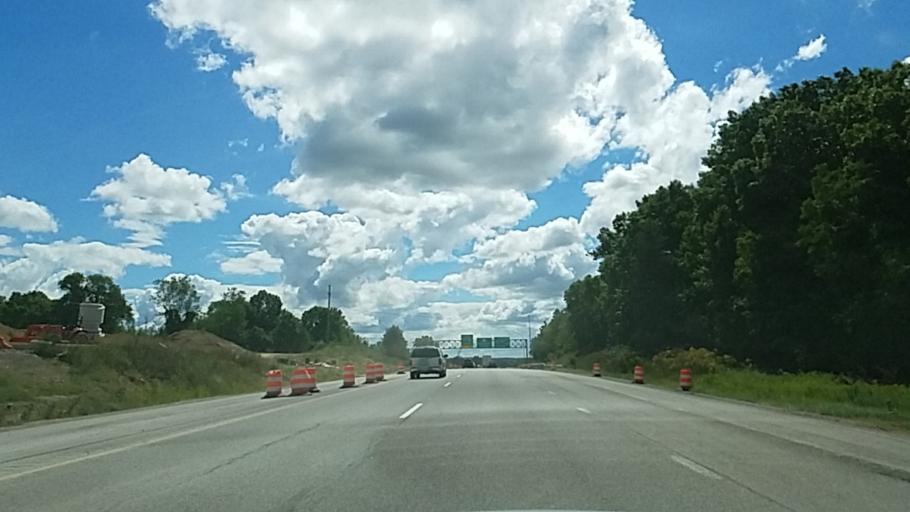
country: US
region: Michigan
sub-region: Livingston County
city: Brighton
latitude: 42.5320
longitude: -83.7532
